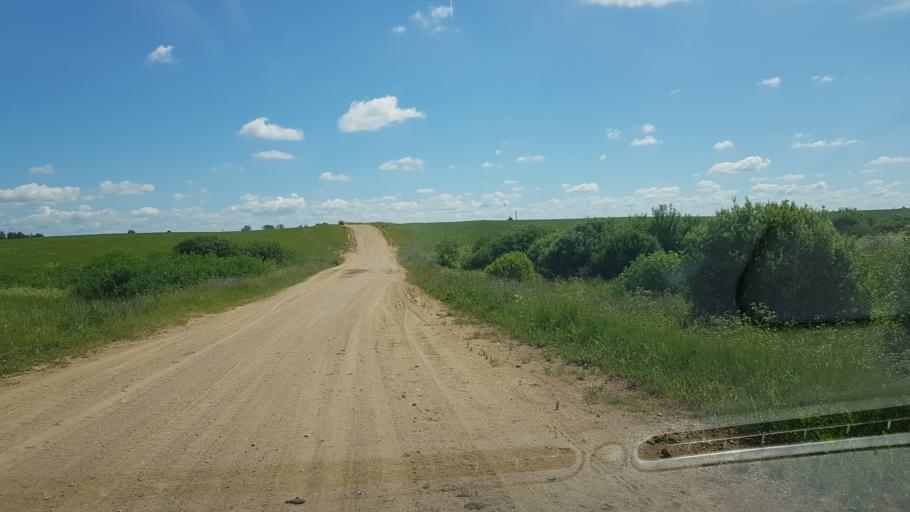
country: BY
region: Vitebsk
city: Dubrowna
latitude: 54.4818
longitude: 30.7865
